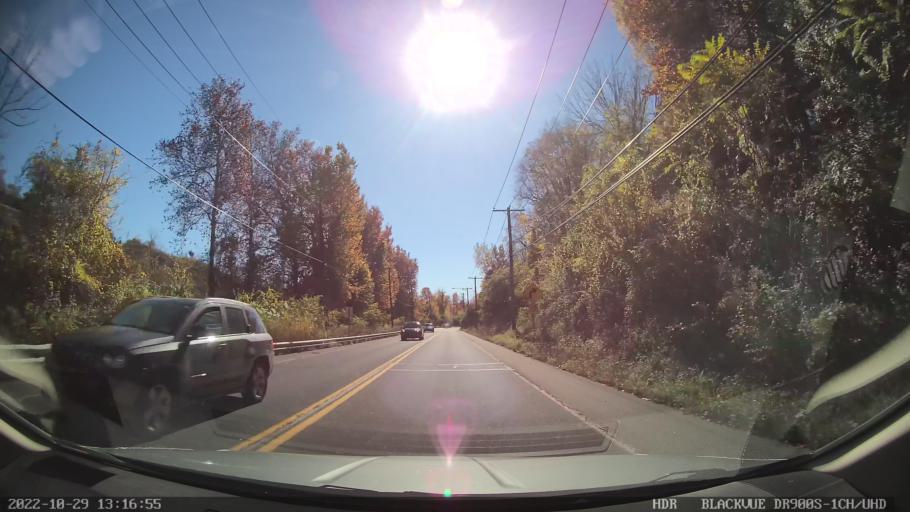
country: US
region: Pennsylvania
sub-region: Northampton County
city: Freemansburg
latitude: 40.6140
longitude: -75.3353
